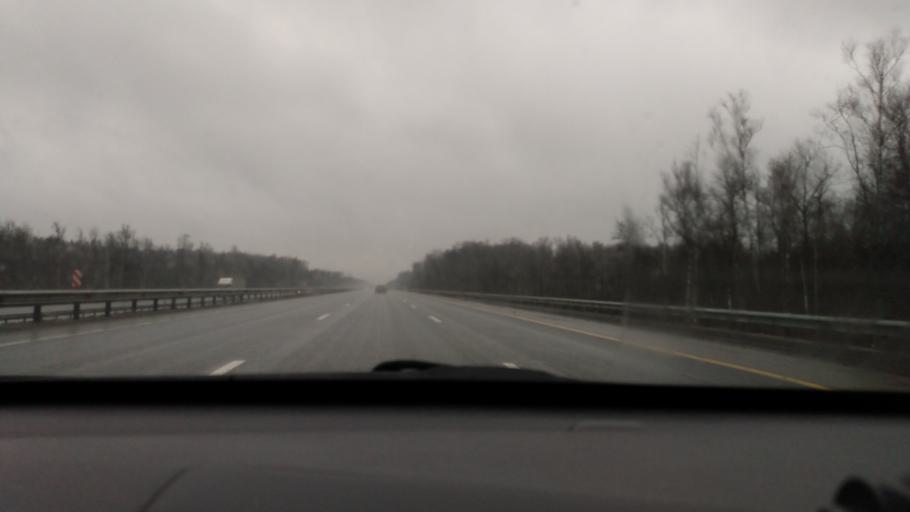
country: RU
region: Moskovskaya
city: Zhilevo
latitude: 54.9523
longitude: 37.9834
